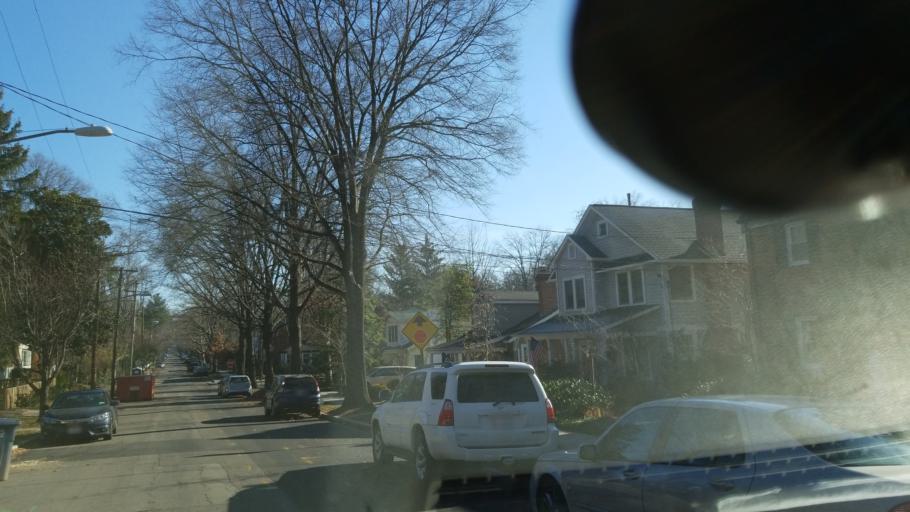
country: US
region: Maryland
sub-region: Montgomery County
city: Friendship Village
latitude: 38.9497
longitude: -77.0954
